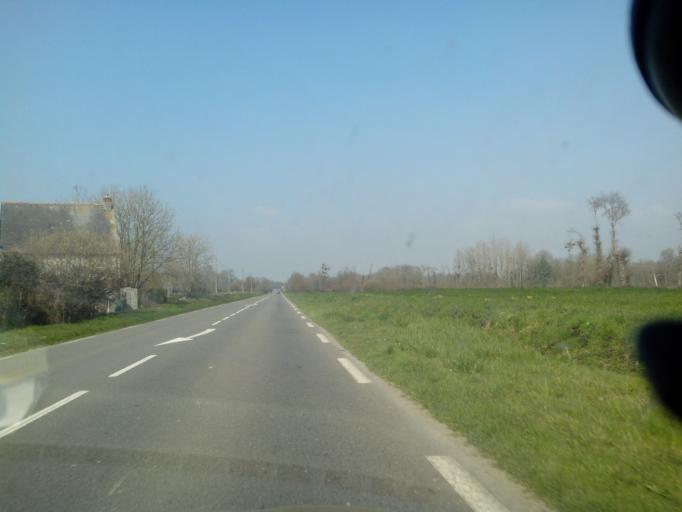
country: FR
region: Brittany
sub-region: Departement d'Ille-et-Vilaine
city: Saint-Meen-le-Grand
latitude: 48.2137
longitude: -2.1765
